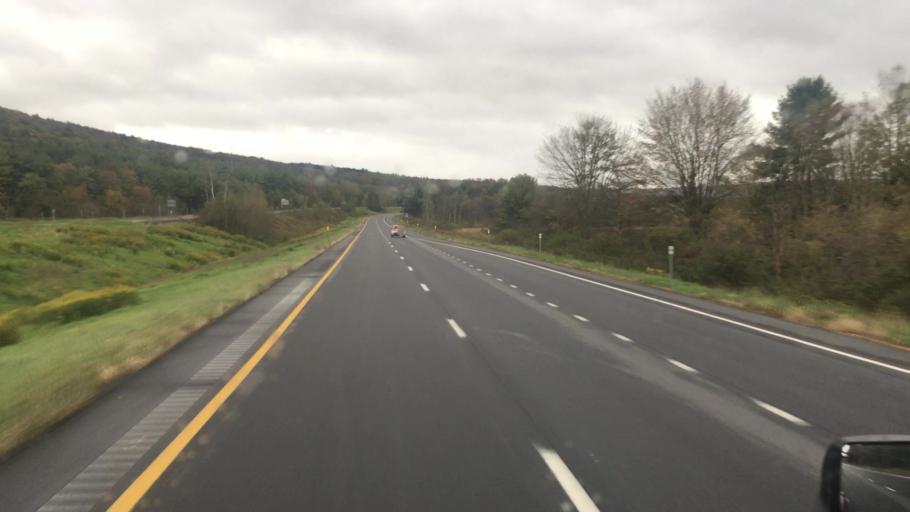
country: US
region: New York
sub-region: Chenango County
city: Bainbridge
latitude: 42.2195
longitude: -75.5139
